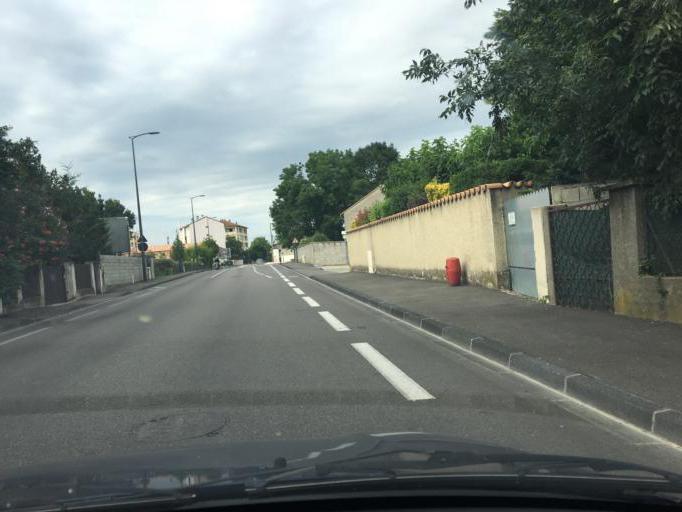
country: FR
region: Rhone-Alpes
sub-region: Departement de la Drome
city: Valence
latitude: 44.9114
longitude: 4.8882
